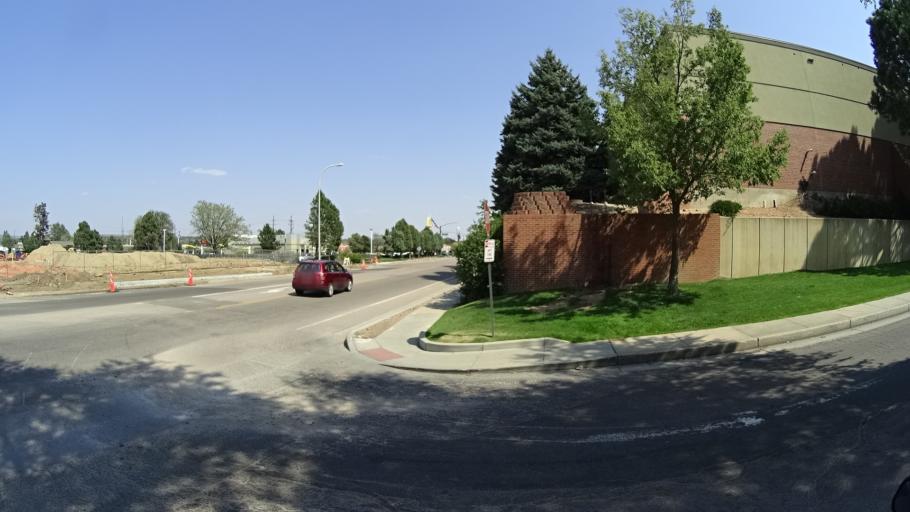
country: US
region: Colorado
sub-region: El Paso County
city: Colorado Springs
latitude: 38.8066
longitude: -104.8240
